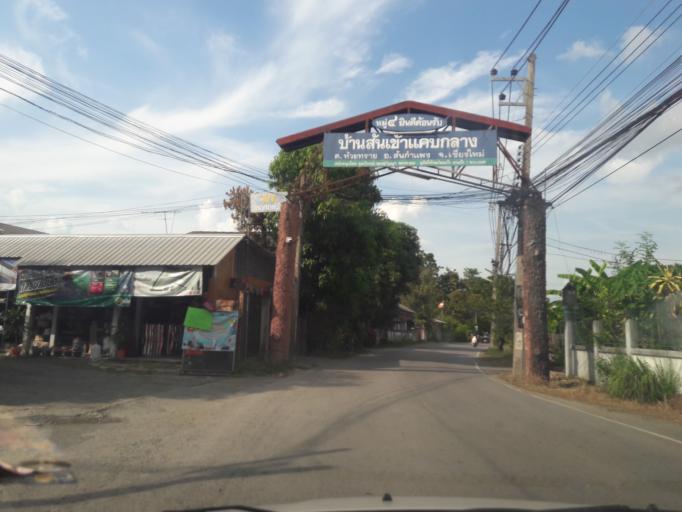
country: TH
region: Chiang Mai
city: San Kamphaeng
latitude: 18.7812
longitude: 99.1588
